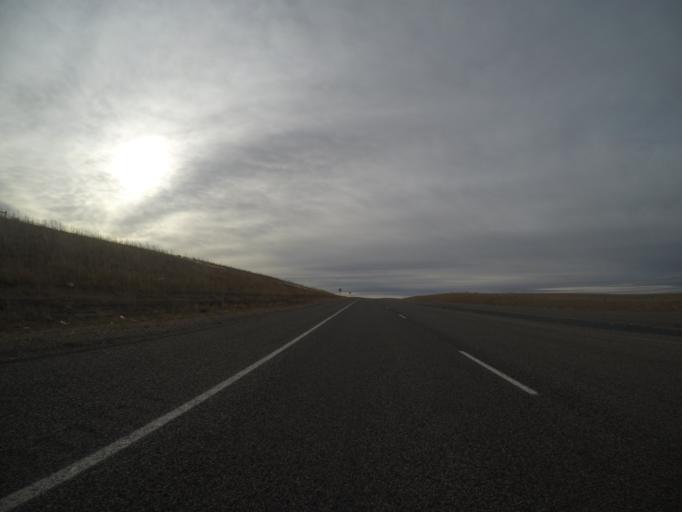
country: US
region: Montana
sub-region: Yellowstone County
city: Laurel
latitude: 45.5577
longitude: -108.8591
